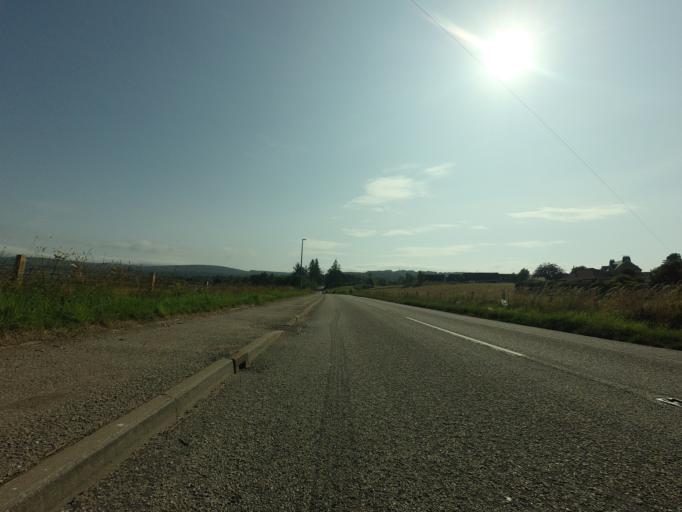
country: GB
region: Scotland
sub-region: Highland
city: Alness
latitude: 57.8849
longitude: -4.3604
